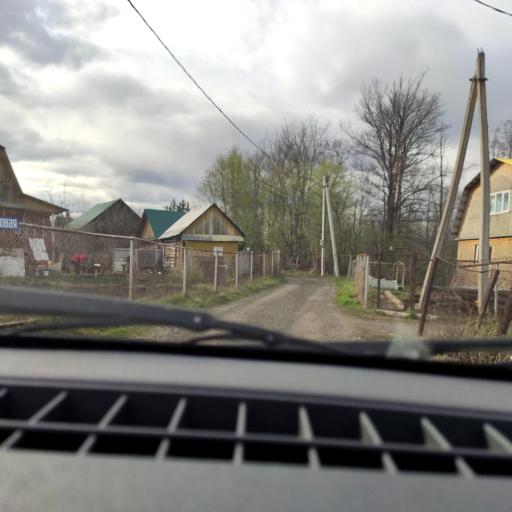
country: RU
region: Bashkortostan
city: Mikhaylovka
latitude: 54.7948
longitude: 55.8384
